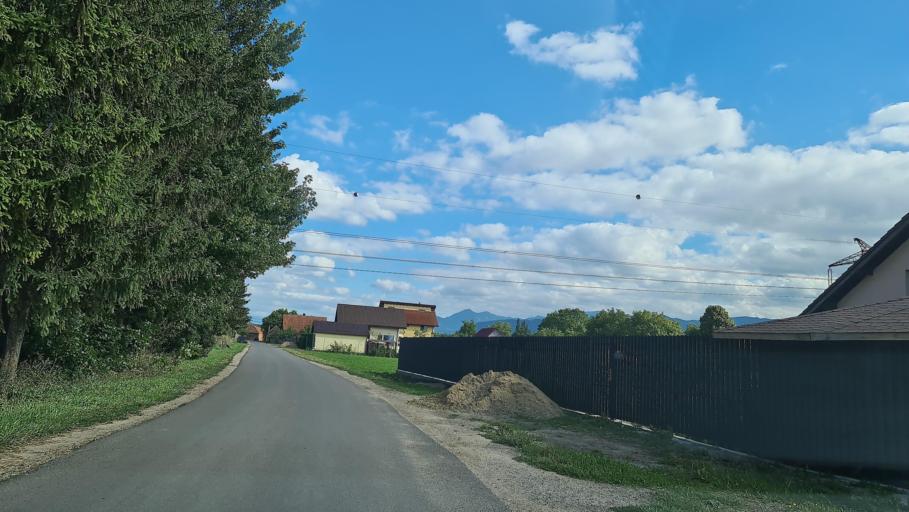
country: RO
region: Brasov
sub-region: Comuna Ghimbav
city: Ghimbav
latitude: 45.6965
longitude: 25.5497
